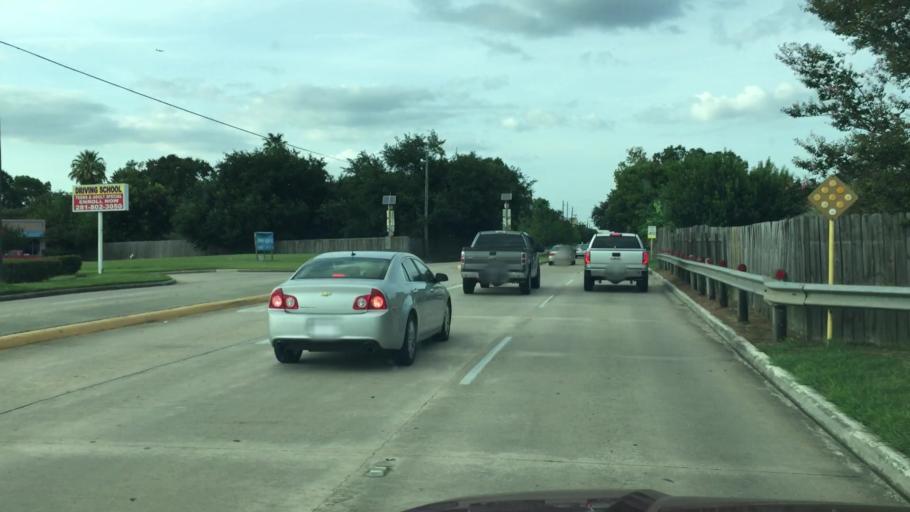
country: US
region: Texas
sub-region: Harris County
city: Hudson
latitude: 29.9735
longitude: -95.4940
